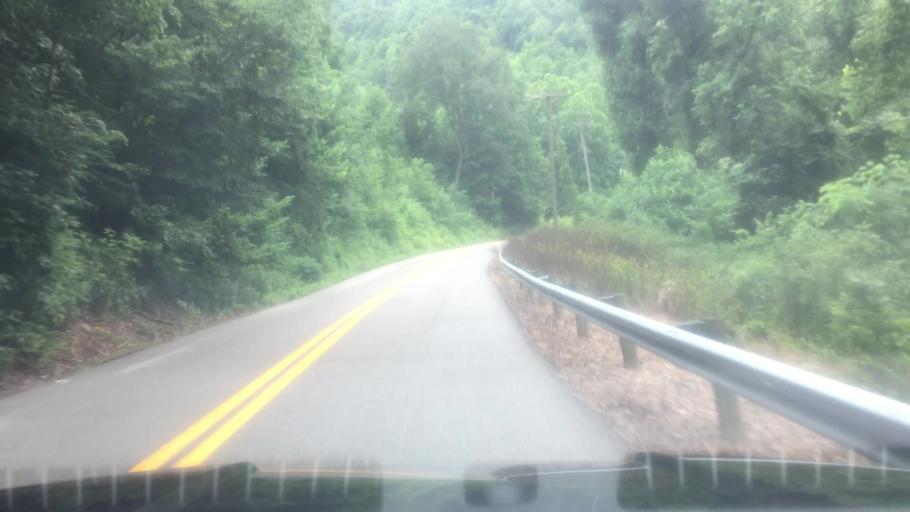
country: US
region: West Virginia
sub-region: Kanawha County
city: Montgomery
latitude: 38.1025
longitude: -81.3817
